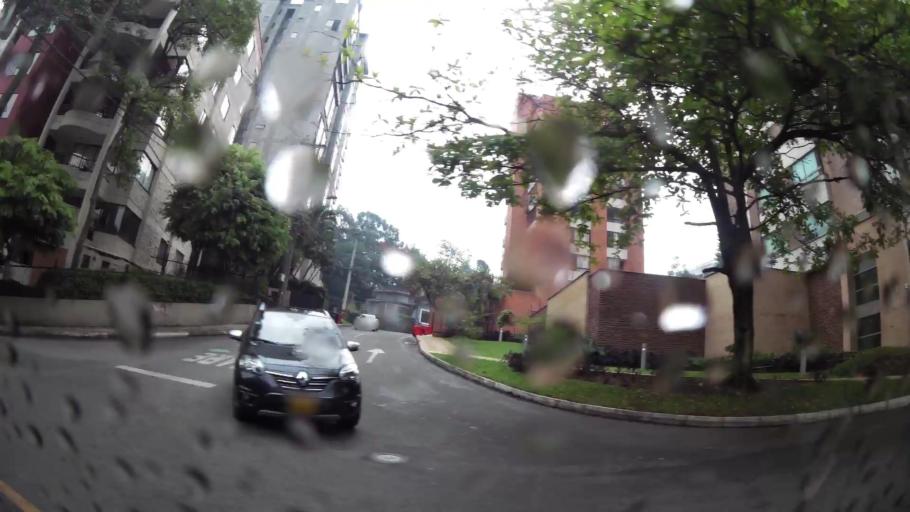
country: CO
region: Antioquia
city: Envigado
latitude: 6.1997
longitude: -75.5680
